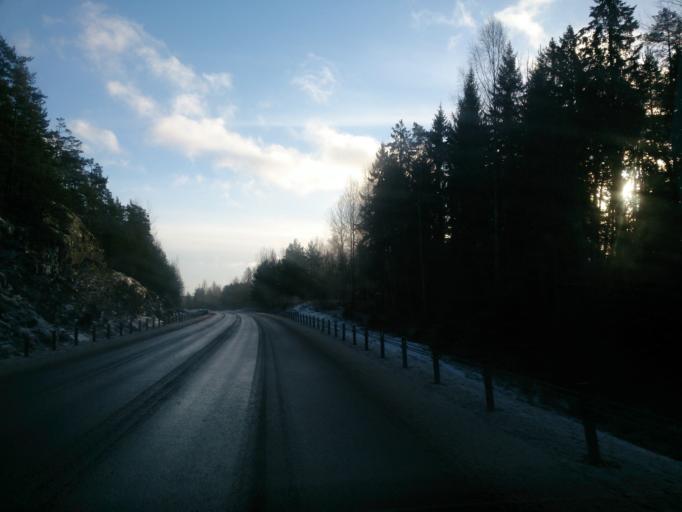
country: SE
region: OEstergoetland
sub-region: Atvidabergs Kommun
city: Atvidaberg
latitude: 58.2401
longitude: 15.9373
